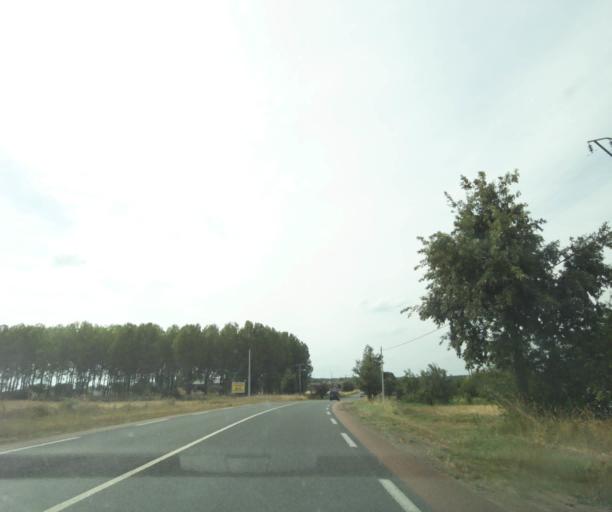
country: FR
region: Pays de la Loire
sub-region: Departement de la Sarthe
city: Luceau
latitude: 47.7463
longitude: 0.3751
